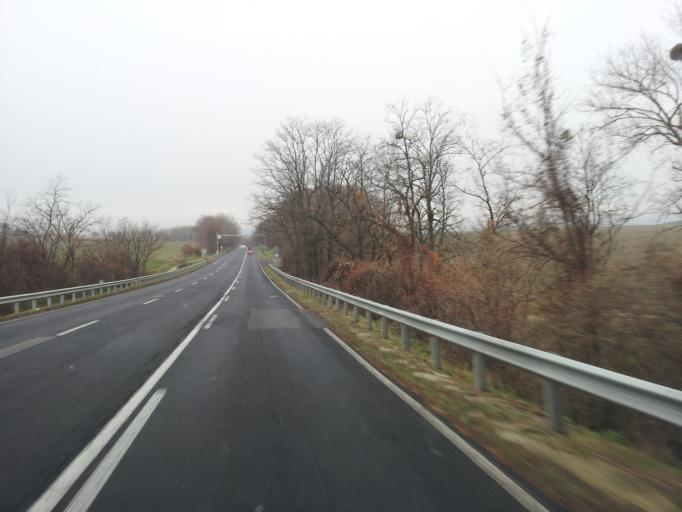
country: HU
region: Veszprem
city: Ajka
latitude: 47.1410
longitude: 17.5732
